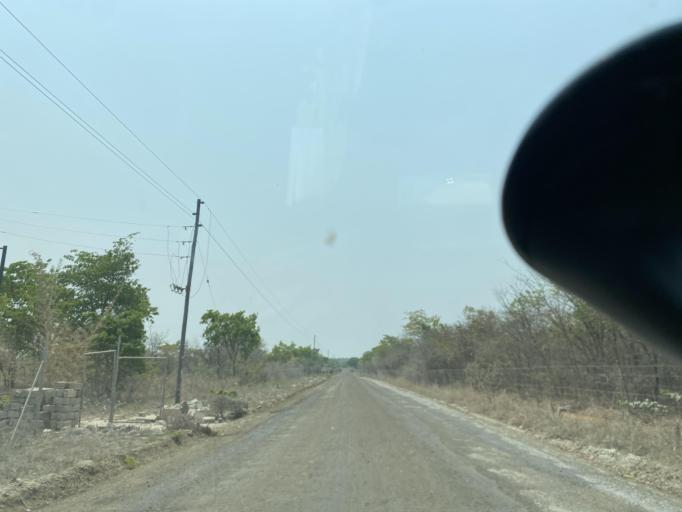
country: ZM
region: Lusaka
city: Lusaka
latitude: -15.5148
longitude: 28.4440
